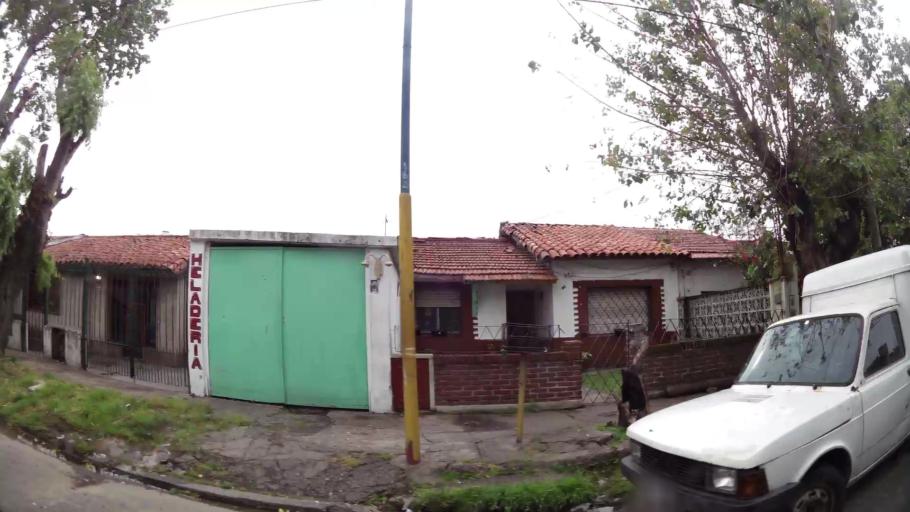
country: AR
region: Buenos Aires
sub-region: Partido de Lanus
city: Lanus
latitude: -34.7047
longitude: -58.3616
